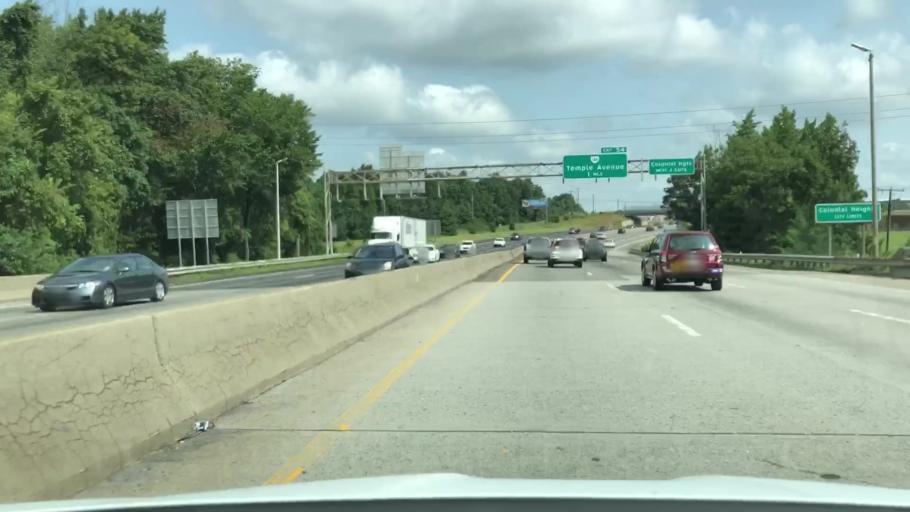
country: US
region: Virginia
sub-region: City of Petersburg
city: Petersburg
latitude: 37.2394
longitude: -77.3953
